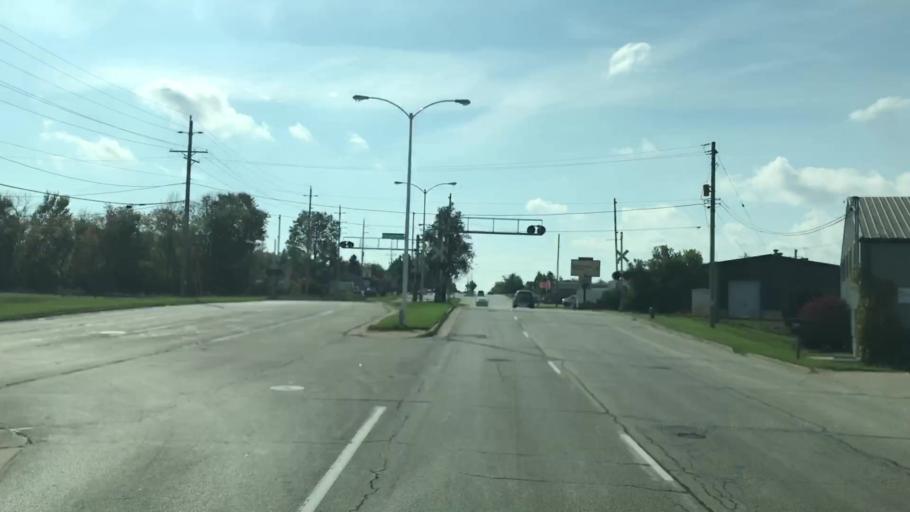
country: US
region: Wisconsin
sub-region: Waukesha County
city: Menomonee Falls
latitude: 43.1770
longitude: -88.0443
